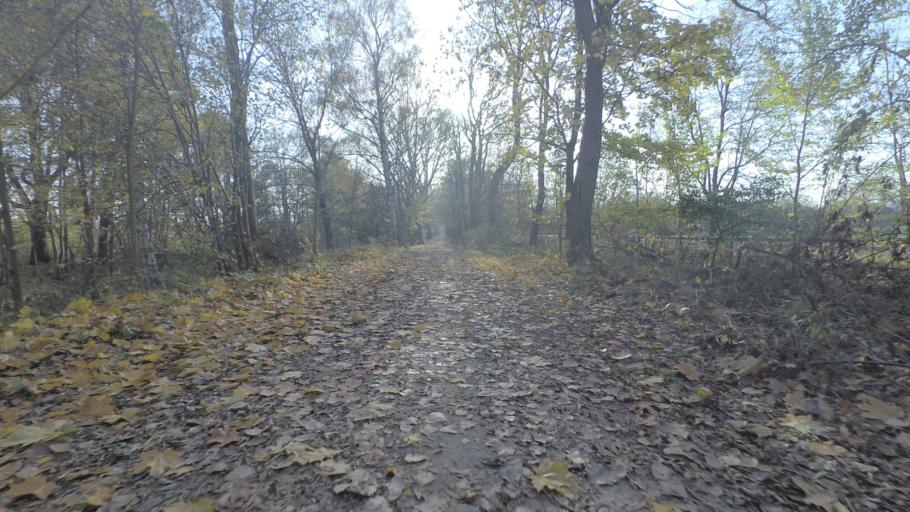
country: DE
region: Brandenburg
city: Am Mellensee
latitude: 52.2015
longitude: 13.4171
